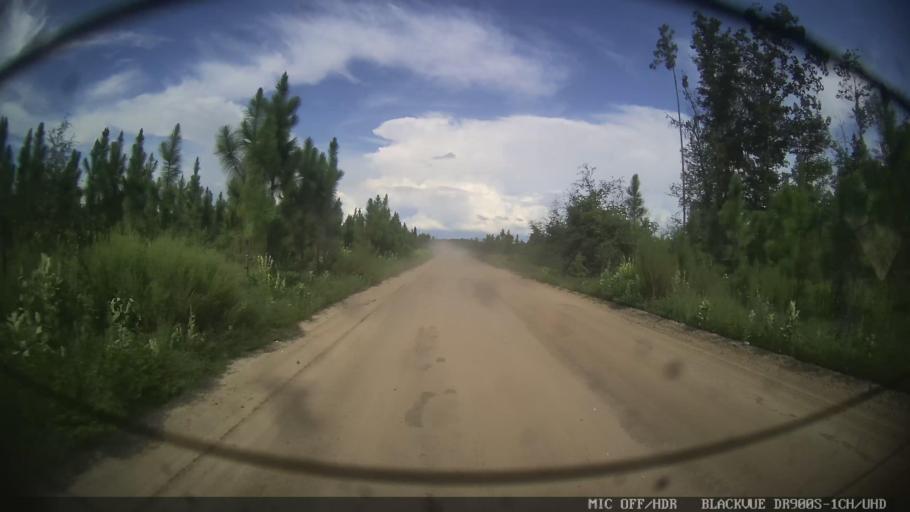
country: US
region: Georgia
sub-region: Echols County
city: Statenville
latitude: 30.6182
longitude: -83.2294
